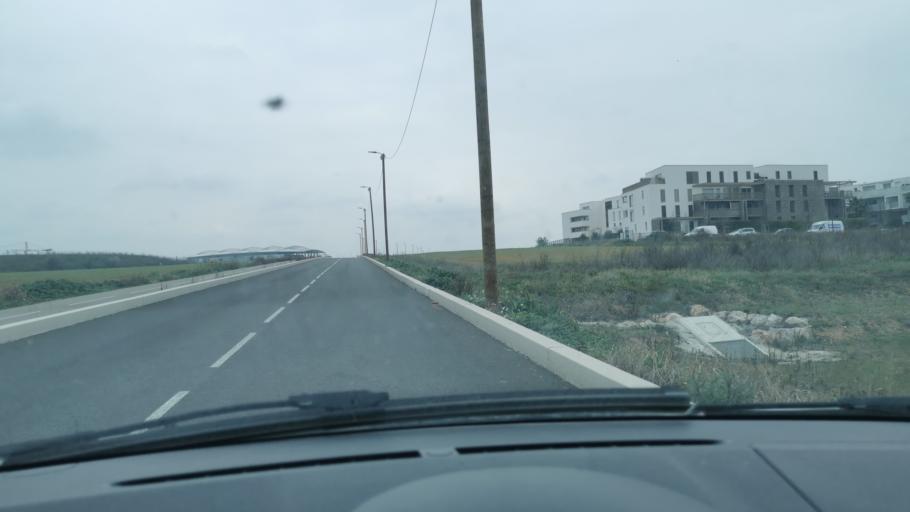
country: FR
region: Languedoc-Roussillon
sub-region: Departement de l'Herault
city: Lattes
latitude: 43.5905
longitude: 3.9192
